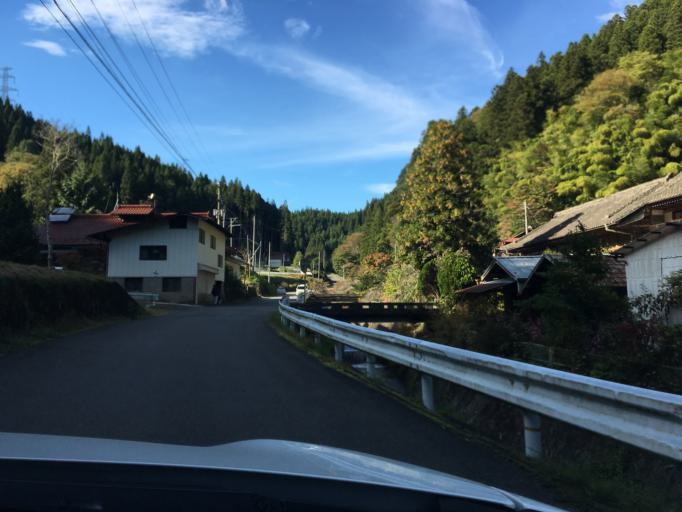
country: JP
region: Fukushima
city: Ishikawa
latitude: 37.1168
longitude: 140.5625
